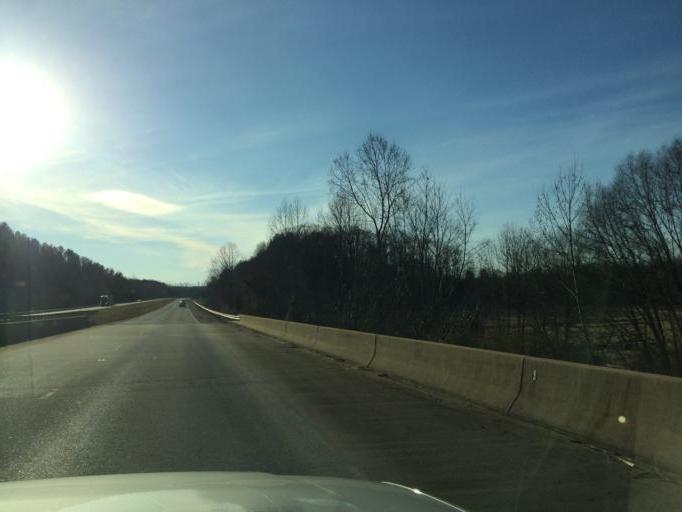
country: US
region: North Carolina
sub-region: Rutherford County
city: Rutherfordton
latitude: 35.2881
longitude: -82.0291
